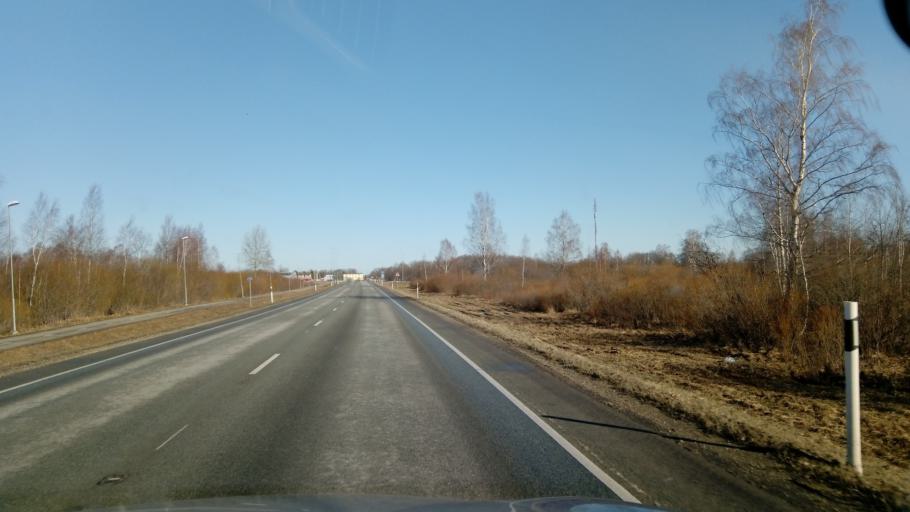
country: EE
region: Laeaene-Virumaa
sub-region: Rakvere linn
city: Rakvere
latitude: 59.3434
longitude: 26.3417
